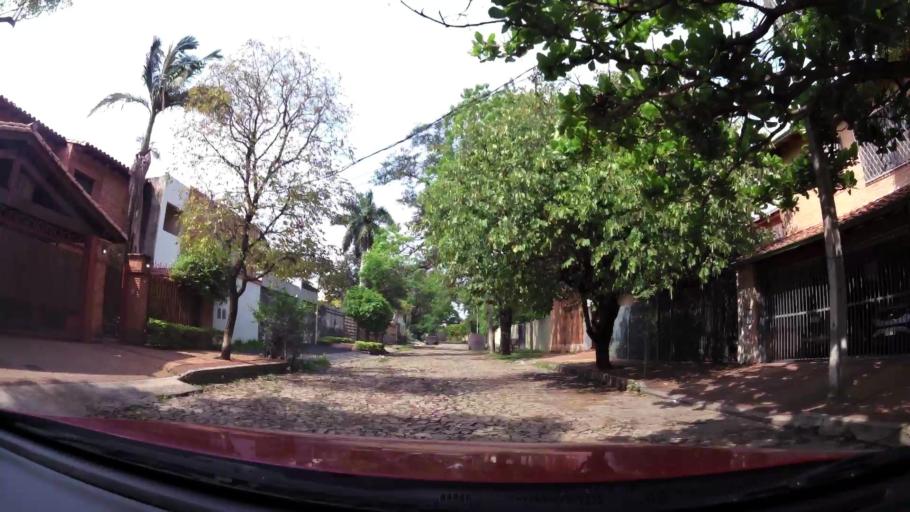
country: PY
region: Asuncion
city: Asuncion
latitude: -25.2674
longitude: -57.5639
